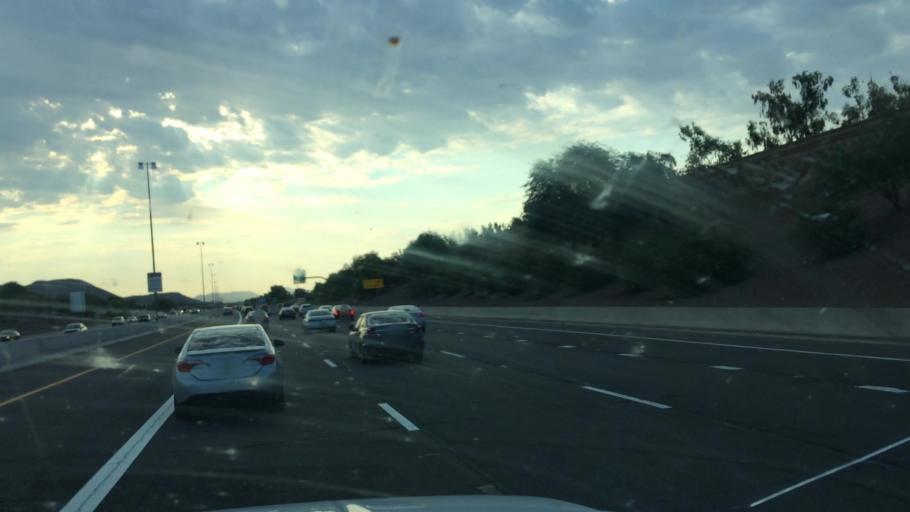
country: US
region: Arizona
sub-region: Maricopa County
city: Peoria
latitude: 33.6711
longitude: -112.2098
